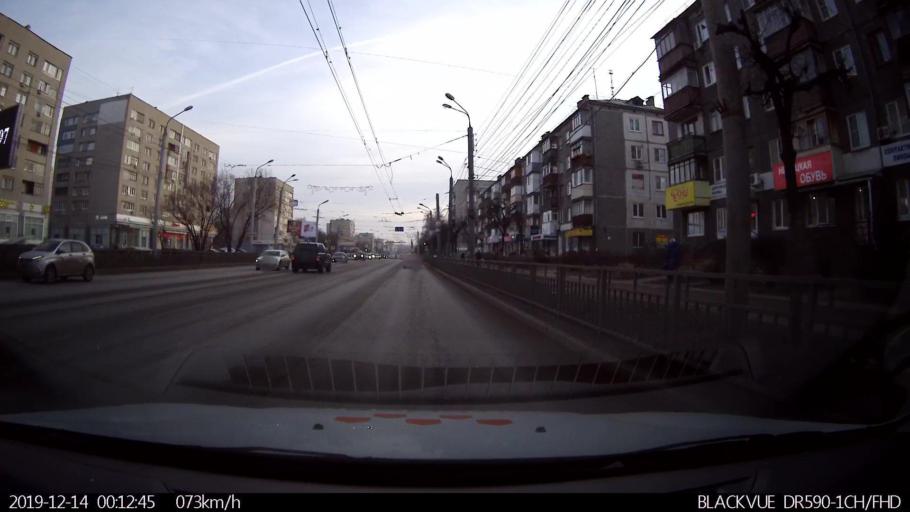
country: RU
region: Nizjnij Novgorod
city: Gorbatovka
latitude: 56.2385
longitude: 43.8662
